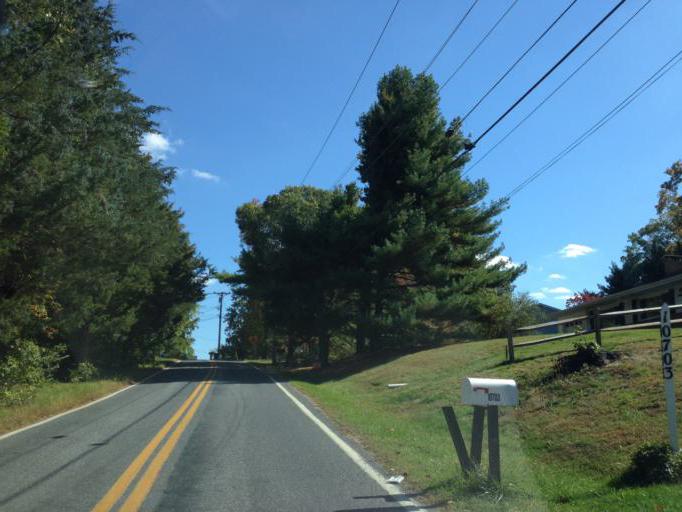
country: US
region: Maryland
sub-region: Howard County
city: North Laurel
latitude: 39.1342
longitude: -76.8834
